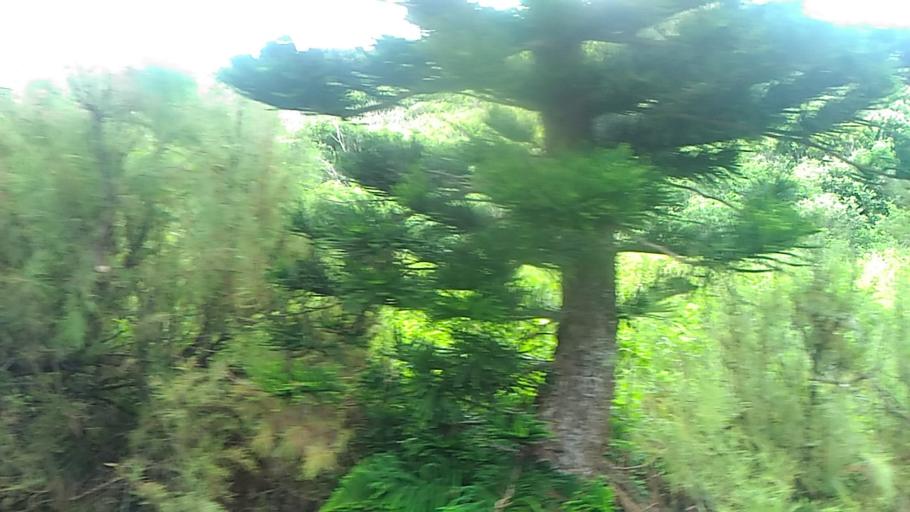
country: TW
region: Taiwan
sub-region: Penghu
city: Ma-kung
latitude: 23.3748
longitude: 119.5054
